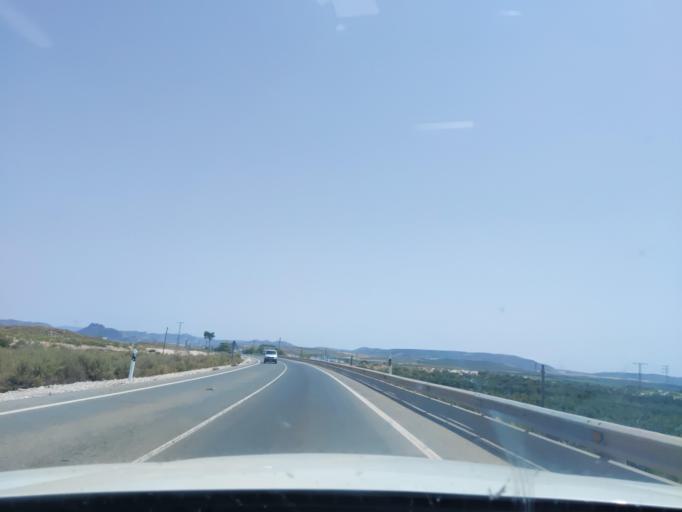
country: ES
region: Castille-La Mancha
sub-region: Provincia de Albacete
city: Hellin
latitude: 38.5006
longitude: -1.6725
